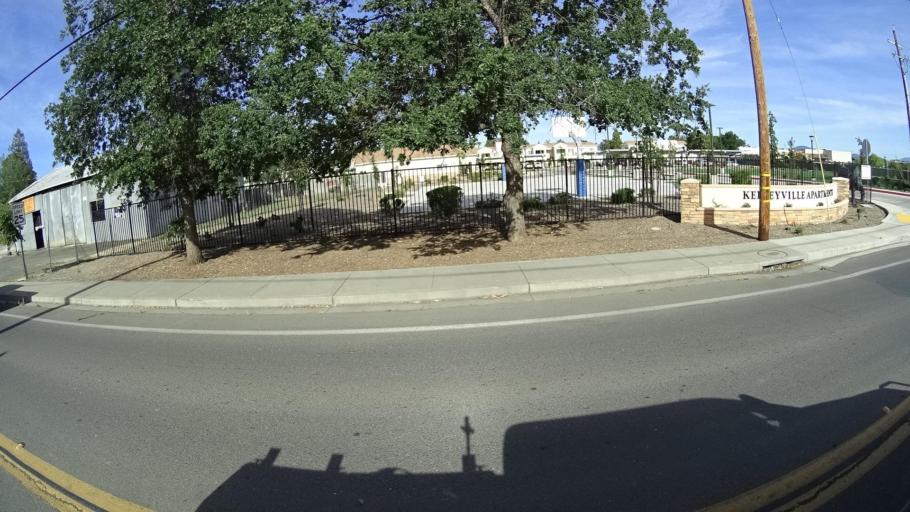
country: US
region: California
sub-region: Lake County
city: Kelseyville
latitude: 38.9797
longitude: -122.8338
